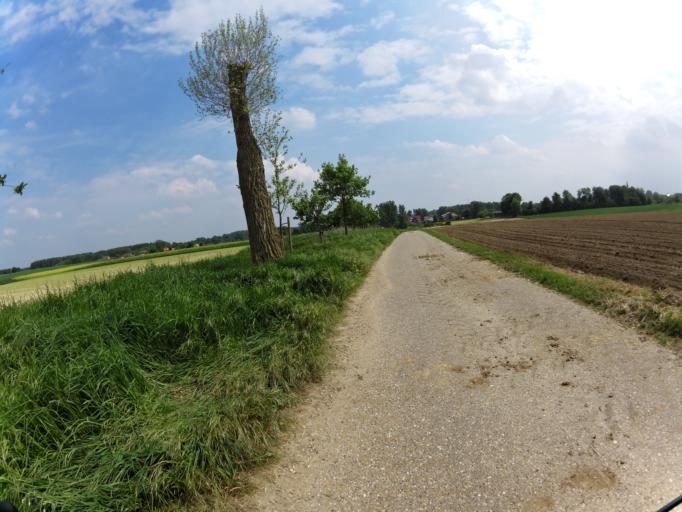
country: DE
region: North Rhine-Westphalia
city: Geilenkirchen
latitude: 51.0054
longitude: 6.1612
